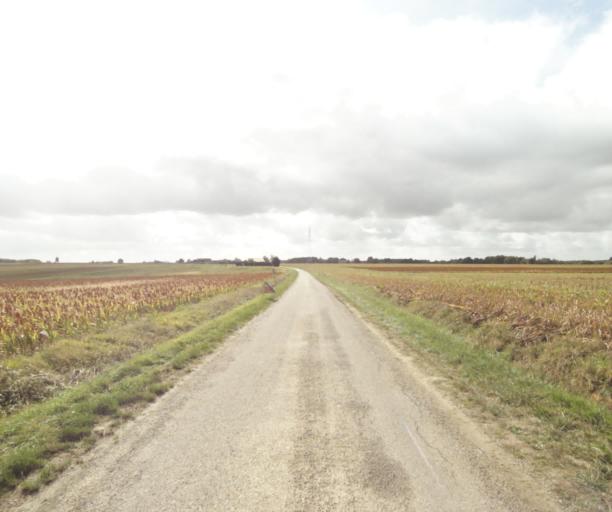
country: FR
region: Midi-Pyrenees
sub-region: Departement du Tarn-et-Garonne
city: Beaumont-de-Lomagne
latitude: 43.8733
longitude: 1.0696
